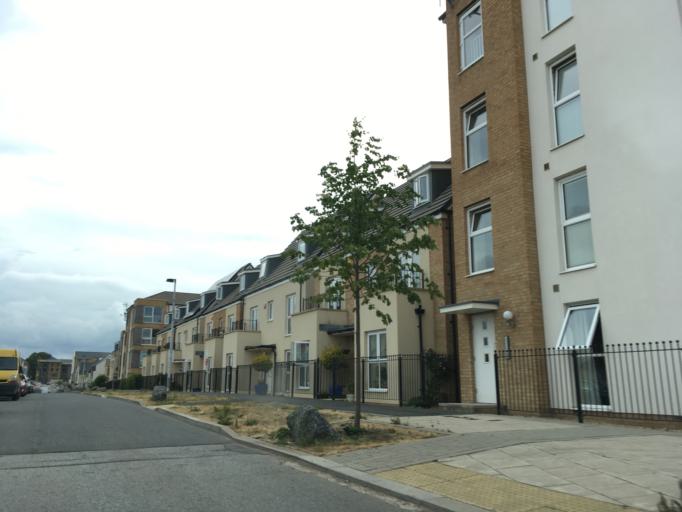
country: GB
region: England
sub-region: South Gloucestershire
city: Almondsbury
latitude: 51.5273
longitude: -2.5757
